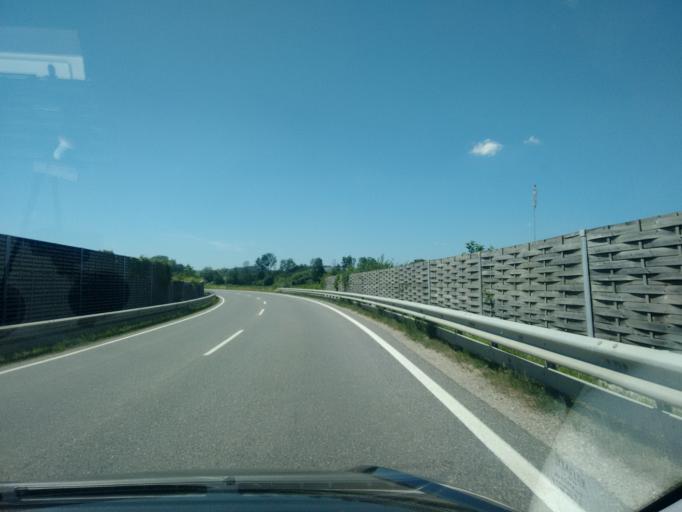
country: AT
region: Lower Austria
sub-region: Politischer Bezirk Sankt Polten
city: Prinzersdorf
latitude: 48.2092
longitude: 15.5147
